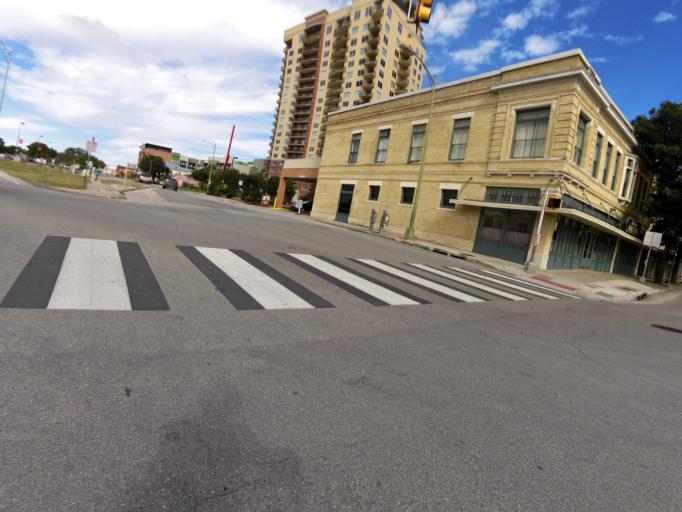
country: US
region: Texas
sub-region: Bexar County
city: San Antonio
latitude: 29.4221
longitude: -98.4804
